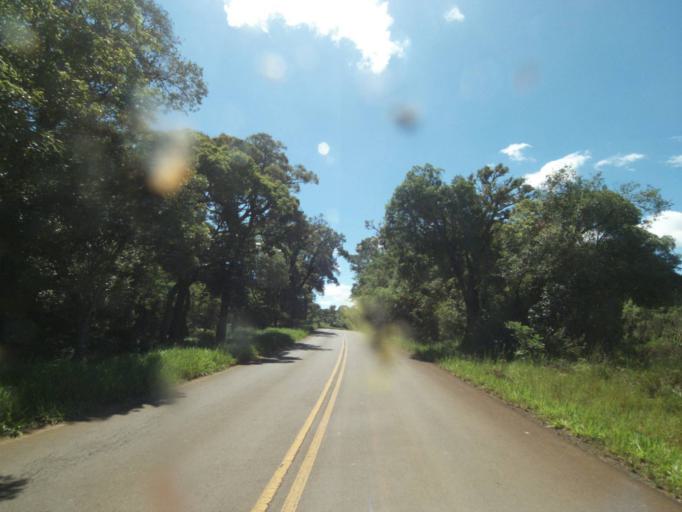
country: BR
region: Parana
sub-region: Pinhao
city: Pinhao
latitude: -25.7953
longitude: -52.0764
